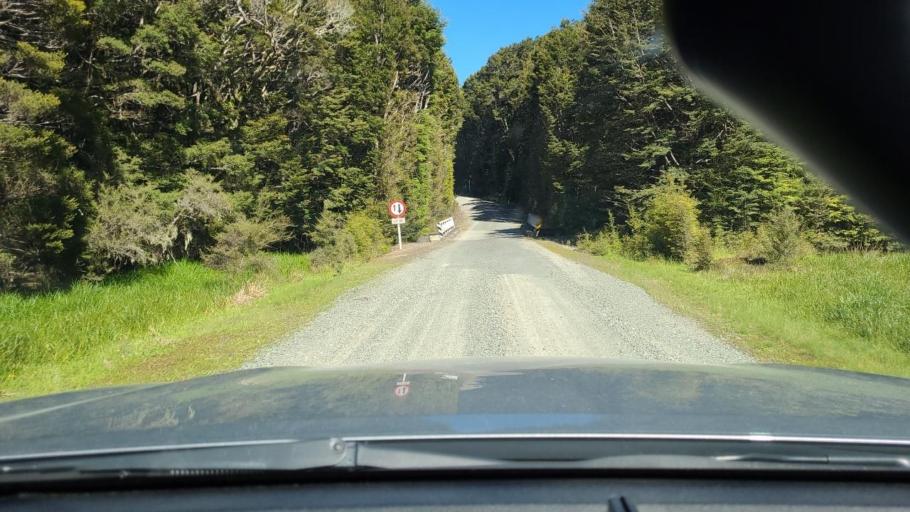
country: NZ
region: Southland
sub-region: Southland District
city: Te Anau
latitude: -46.0075
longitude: 167.4556
